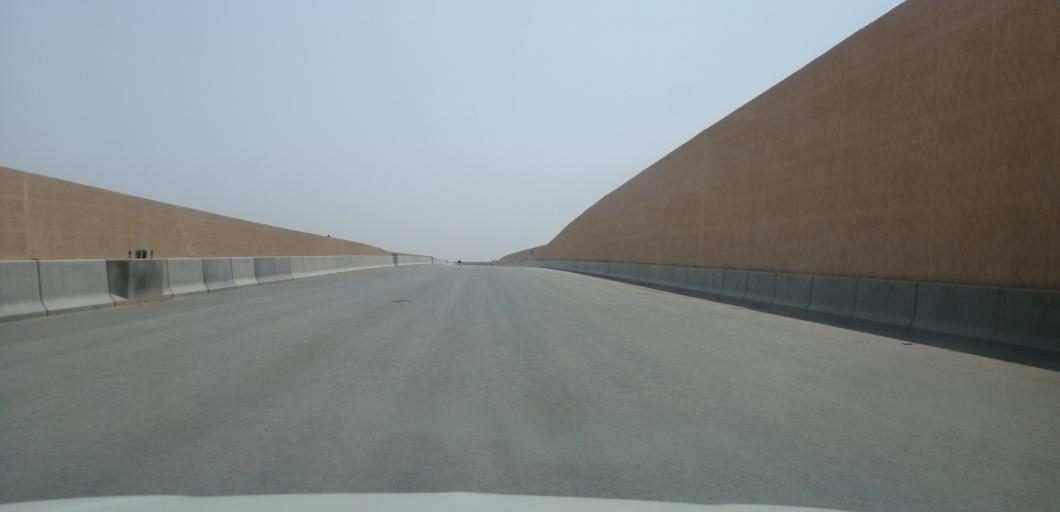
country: KW
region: Muhafazat al Jahra'
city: Al Jahra'
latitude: 29.4537
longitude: 47.5508
